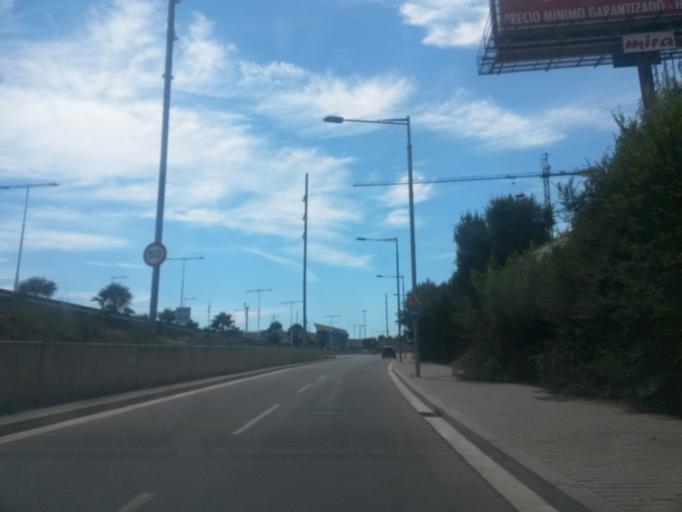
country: ES
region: Catalonia
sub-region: Provincia de Barcelona
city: Sant Adria de Besos
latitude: 41.4153
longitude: 2.2249
